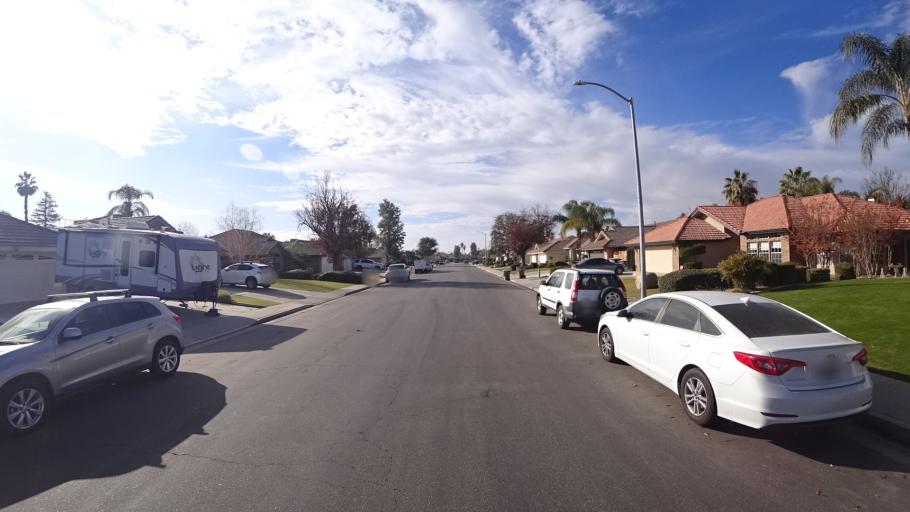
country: US
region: California
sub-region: Kern County
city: Greenacres
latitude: 35.3922
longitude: -119.1115
